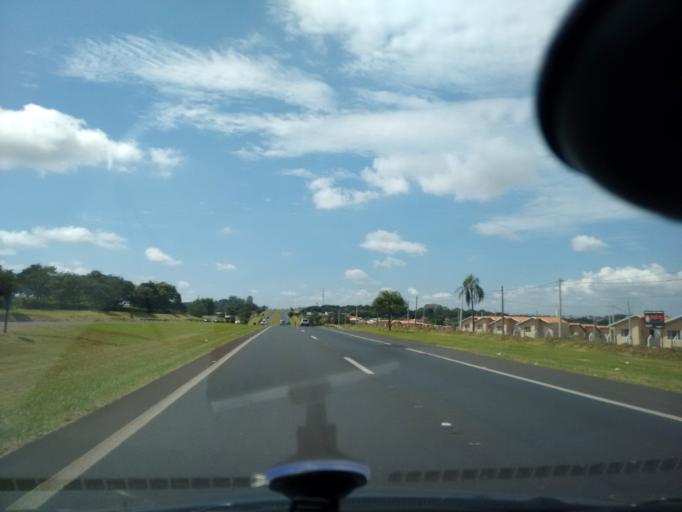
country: BR
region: Sao Paulo
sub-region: Ibate
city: Ibate
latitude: -21.9710
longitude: -47.9501
